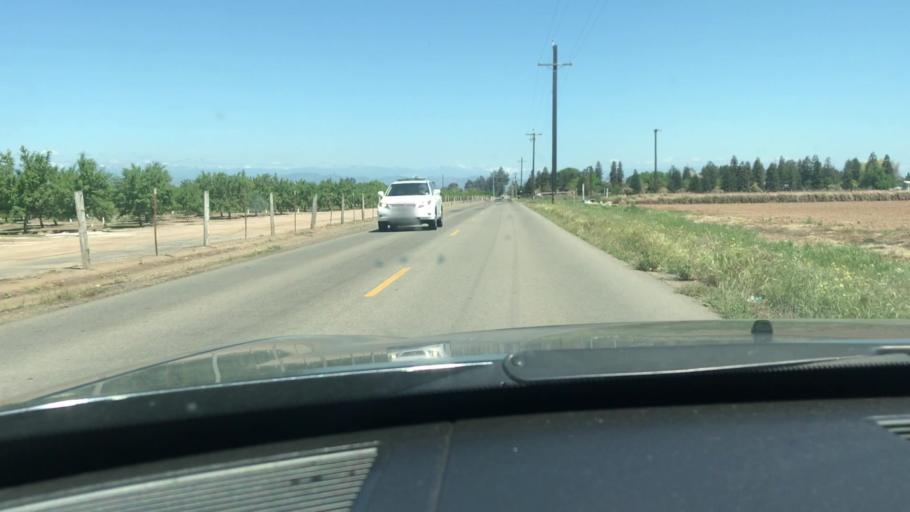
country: US
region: California
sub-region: Fresno County
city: Clovis
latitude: 36.8811
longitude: -119.7035
